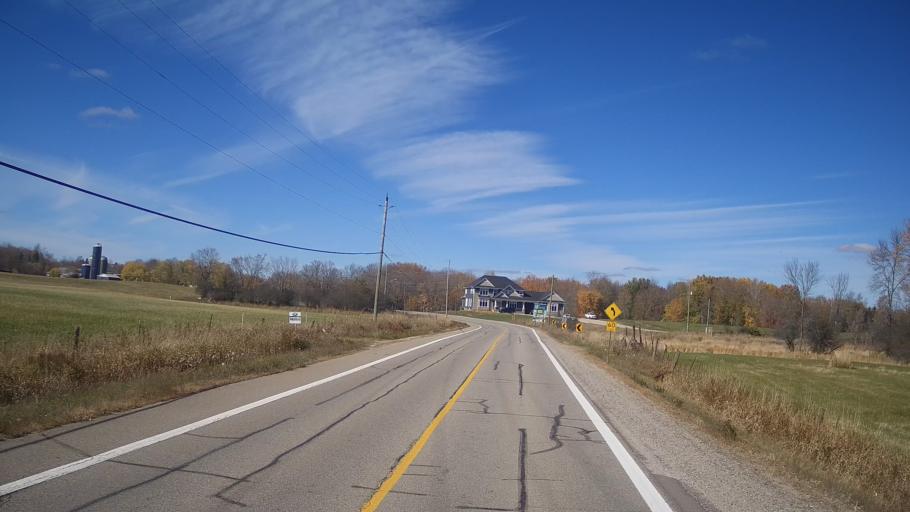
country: CA
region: Ontario
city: Perth
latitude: 44.8737
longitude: -76.2972
